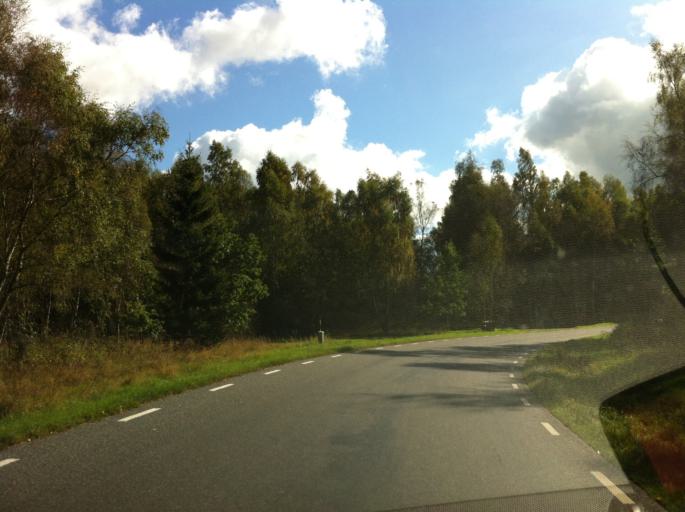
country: SE
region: Skane
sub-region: Kristianstads Kommun
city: Degeberga
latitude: 55.7421
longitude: 13.9389
